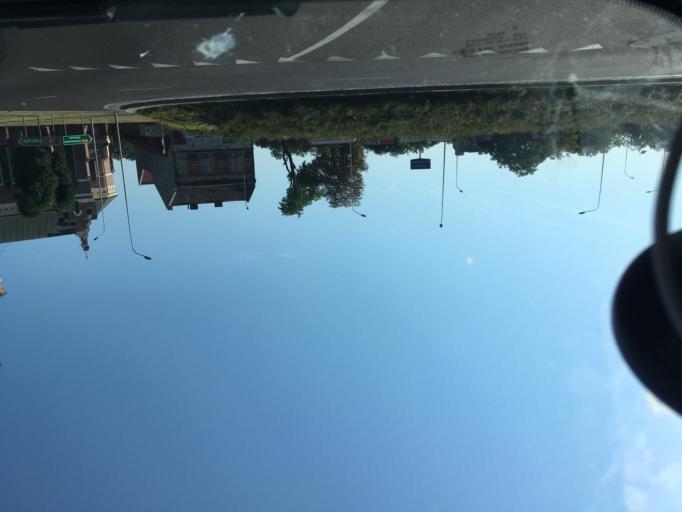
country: PL
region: Subcarpathian Voivodeship
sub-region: Przemysl
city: Przemysl
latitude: 49.7837
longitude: 22.7967
